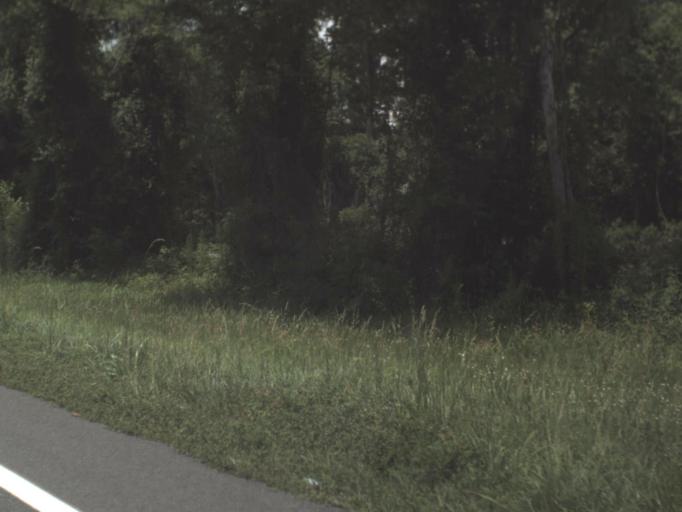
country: US
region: Florida
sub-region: Hamilton County
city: Jasper
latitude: 30.4626
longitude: -82.8988
